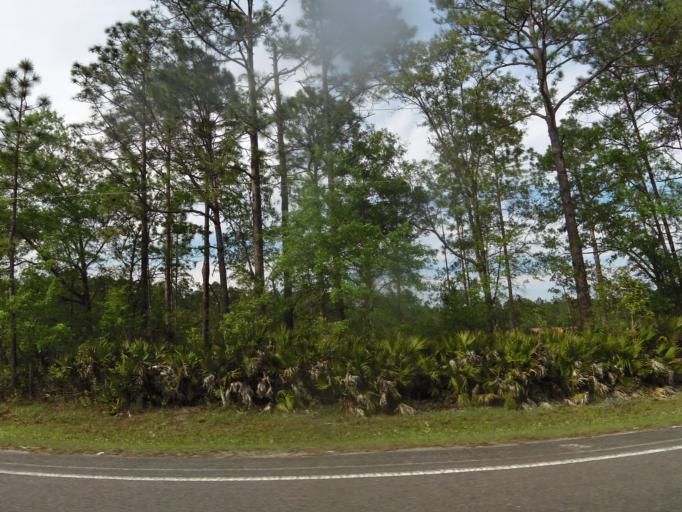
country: US
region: Florida
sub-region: Nassau County
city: Yulee
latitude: 30.6928
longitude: -81.6833
